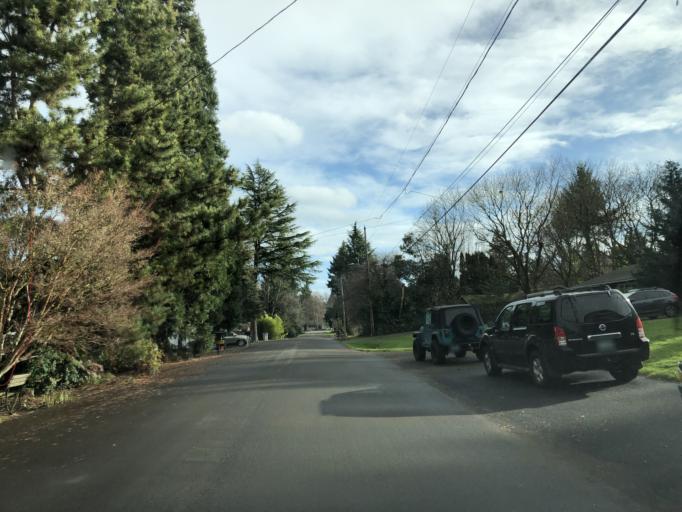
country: US
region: Oregon
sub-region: Washington County
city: Tigard
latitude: 45.4253
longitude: -122.7889
